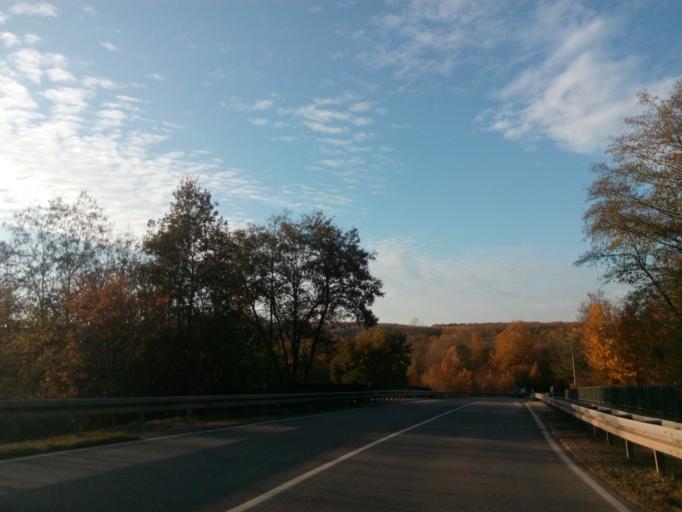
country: DE
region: Saarland
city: Sulzbach
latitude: 49.2856
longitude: 7.0090
